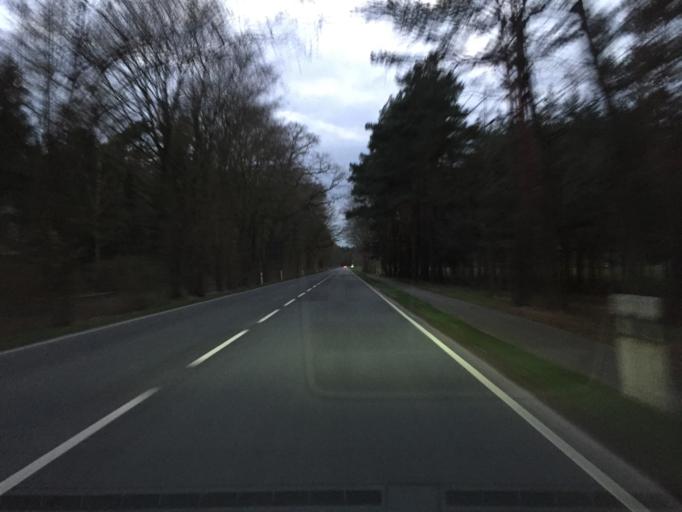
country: DE
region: Lower Saxony
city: Heemsen
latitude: 52.6615
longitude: 9.2710
